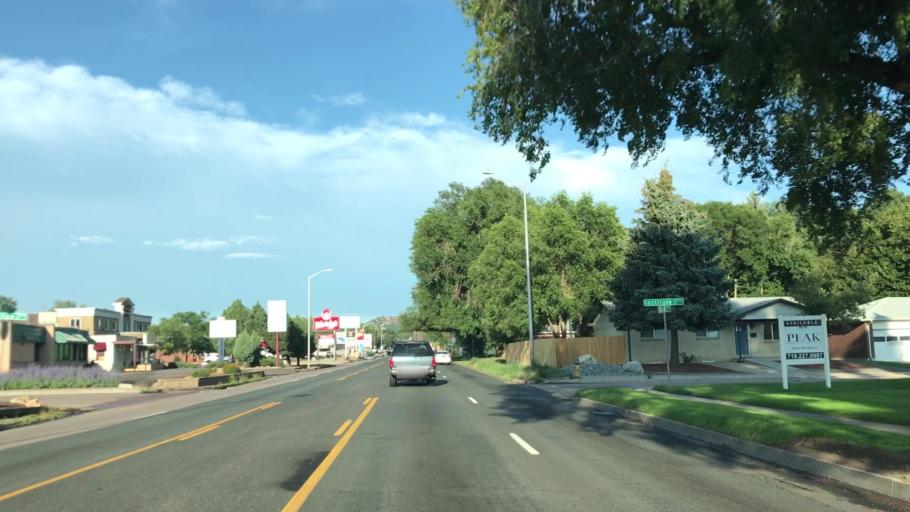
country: US
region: Colorado
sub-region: El Paso County
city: Colorado Springs
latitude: 38.8741
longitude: -104.8081
